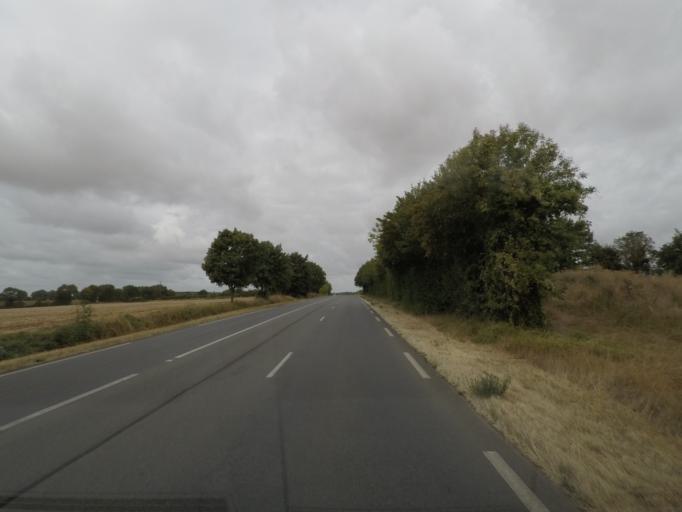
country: FR
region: Poitou-Charentes
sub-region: Departement des Deux-Sevres
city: Thorigne
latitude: 46.2808
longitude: -0.2545
